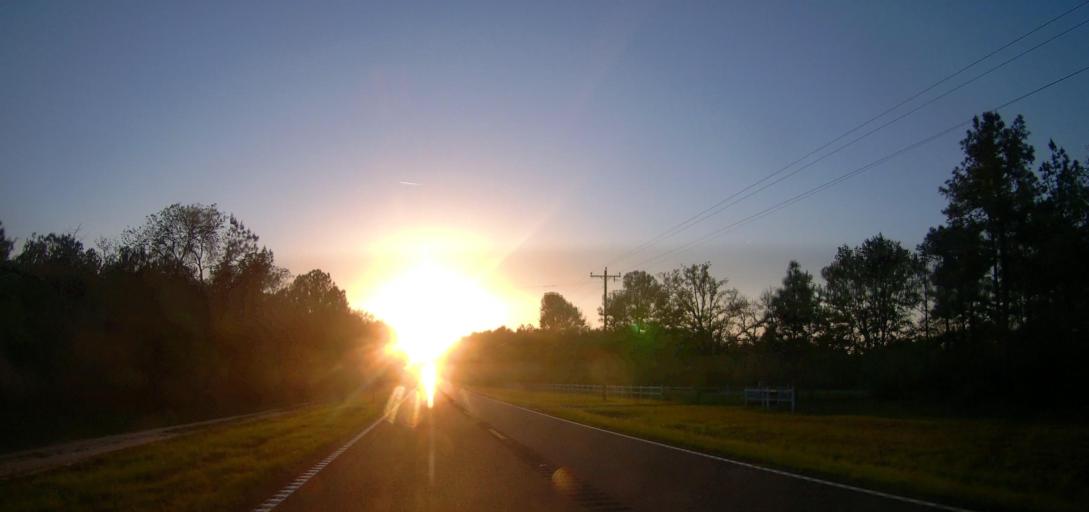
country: US
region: Georgia
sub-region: Marion County
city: Buena Vista
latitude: 32.4423
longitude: -84.6109
